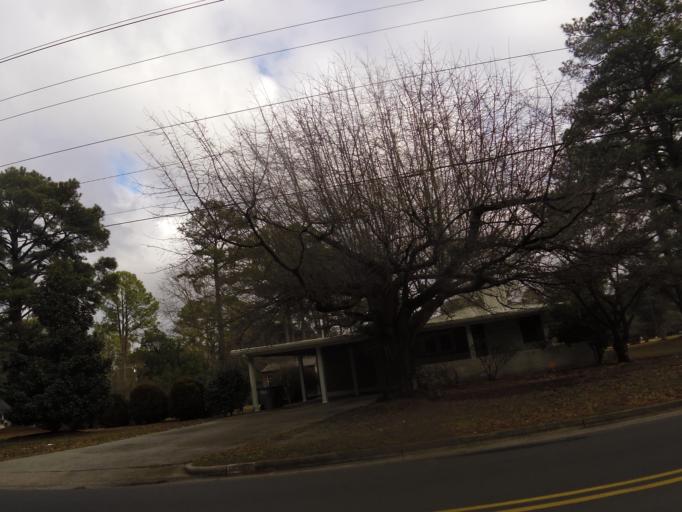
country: US
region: North Carolina
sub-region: Nash County
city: Rocky Mount
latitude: 35.9558
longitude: -77.8487
